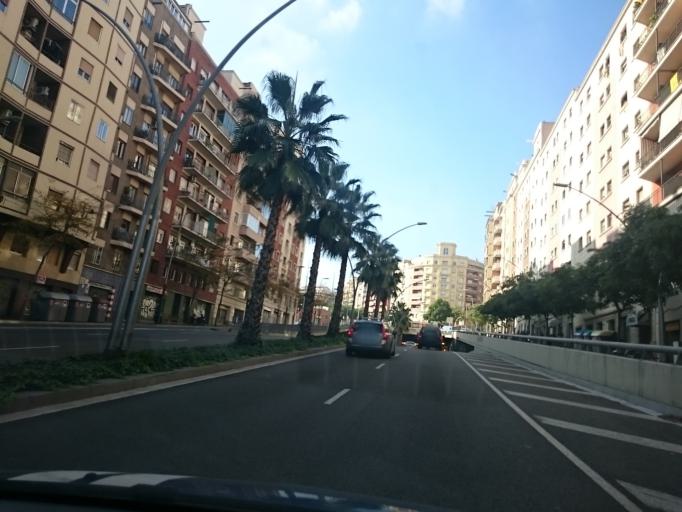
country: ES
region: Catalonia
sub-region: Provincia de Barcelona
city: Horta-Guinardo
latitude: 41.4120
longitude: 2.1640
